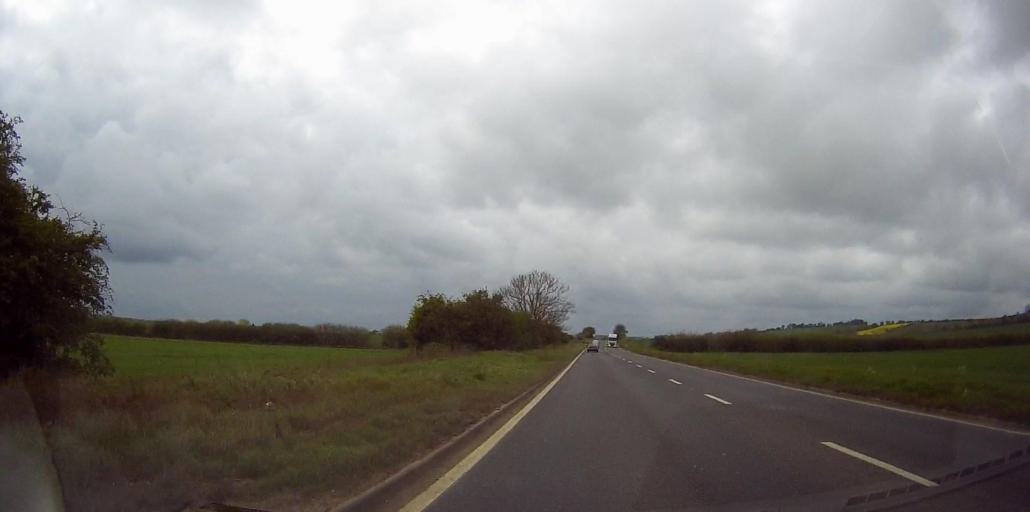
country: GB
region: England
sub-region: Kent
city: Lenham
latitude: 51.2320
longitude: 0.7450
